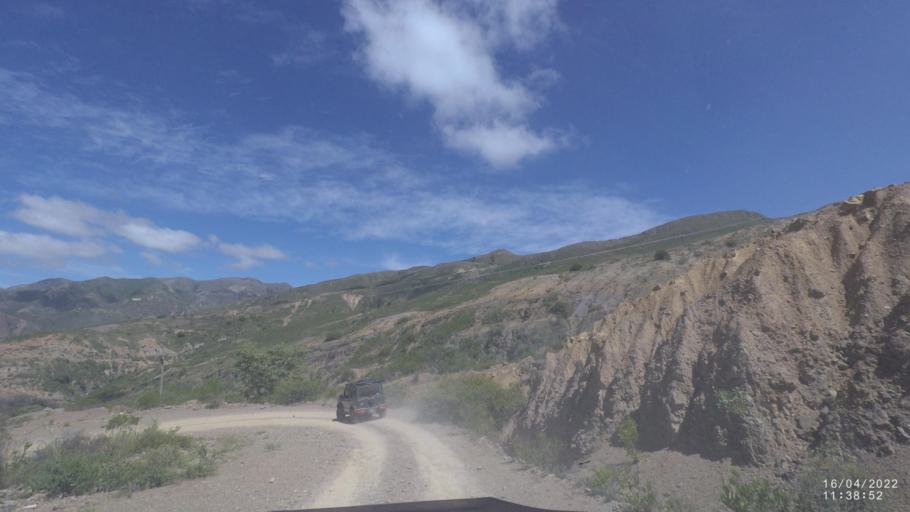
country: BO
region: Cochabamba
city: Mizque
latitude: -17.9652
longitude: -65.6381
